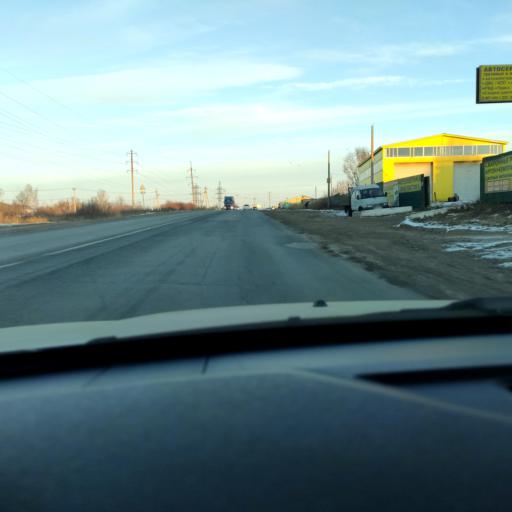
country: RU
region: Samara
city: Smyshlyayevka
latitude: 53.2465
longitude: 50.4753
